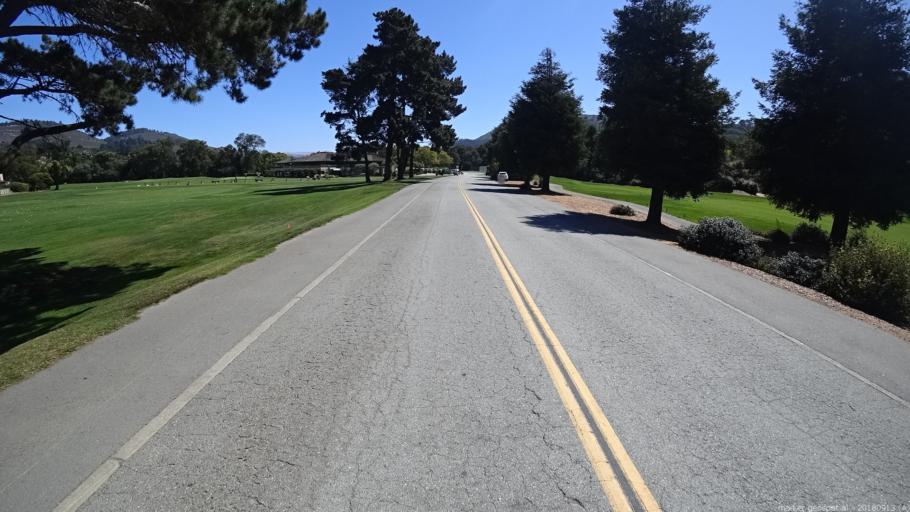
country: US
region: California
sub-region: Monterey County
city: Carmel-by-the-Sea
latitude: 36.5310
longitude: -121.8610
